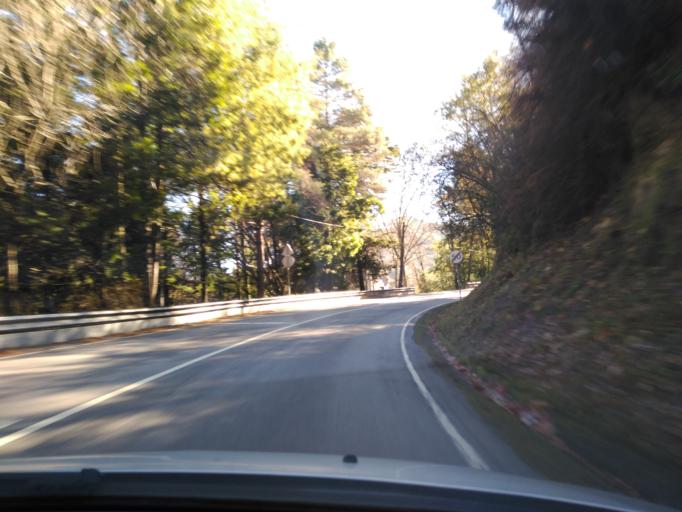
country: PT
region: Braga
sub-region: Cabeceiras de Basto
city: Cabeceiras de Basto
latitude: 41.6783
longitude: -7.9846
